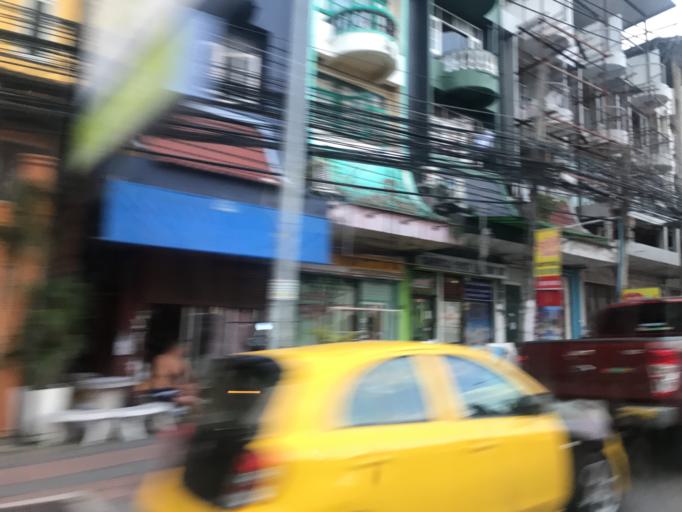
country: TH
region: Chon Buri
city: Phatthaya
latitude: 12.9190
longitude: 100.8718
